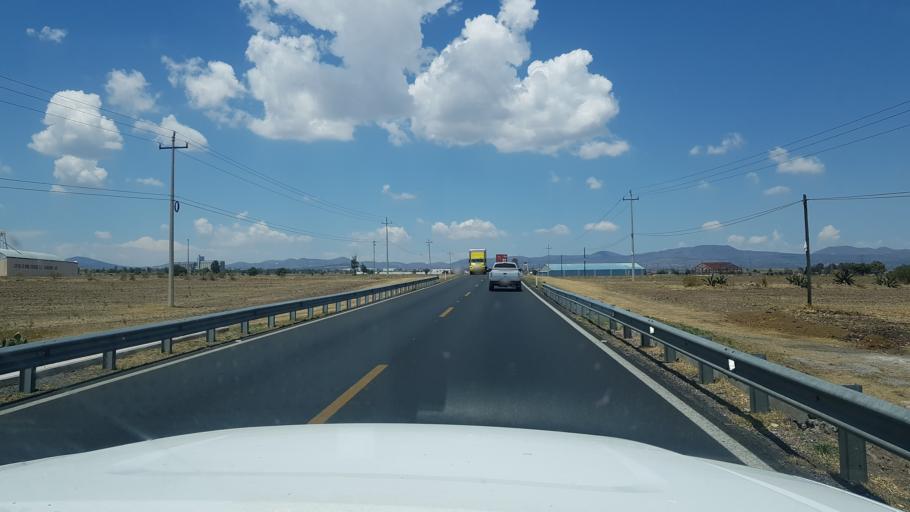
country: MX
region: Hidalgo
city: Calpulalpan
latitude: 19.5786
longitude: -98.5234
